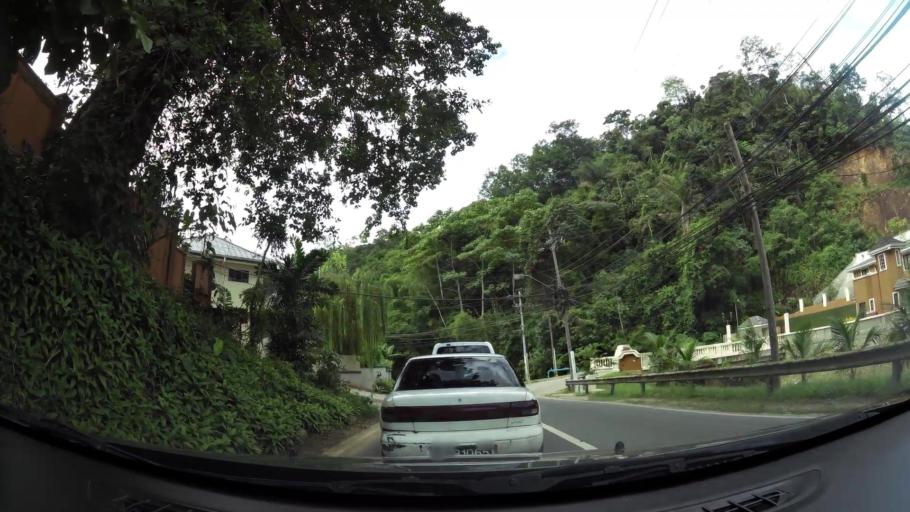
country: TT
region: Diego Martin
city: Petit Valley
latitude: 10.7036
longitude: -61.5122
